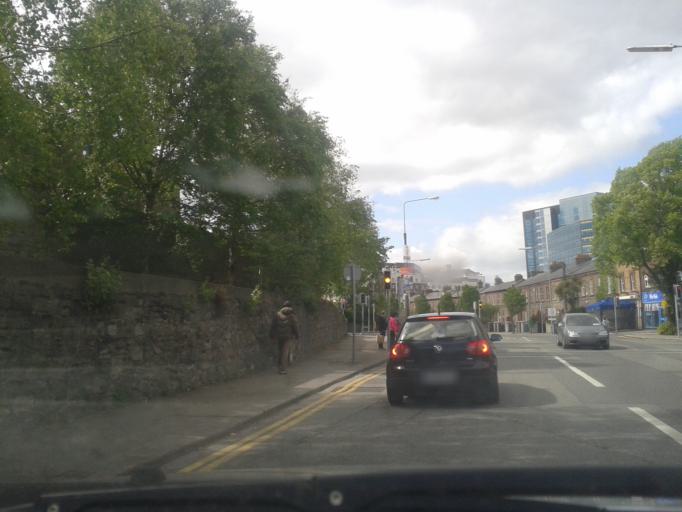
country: IE
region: Leinster
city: Ringsend
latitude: 53.3368
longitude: -6.2341
